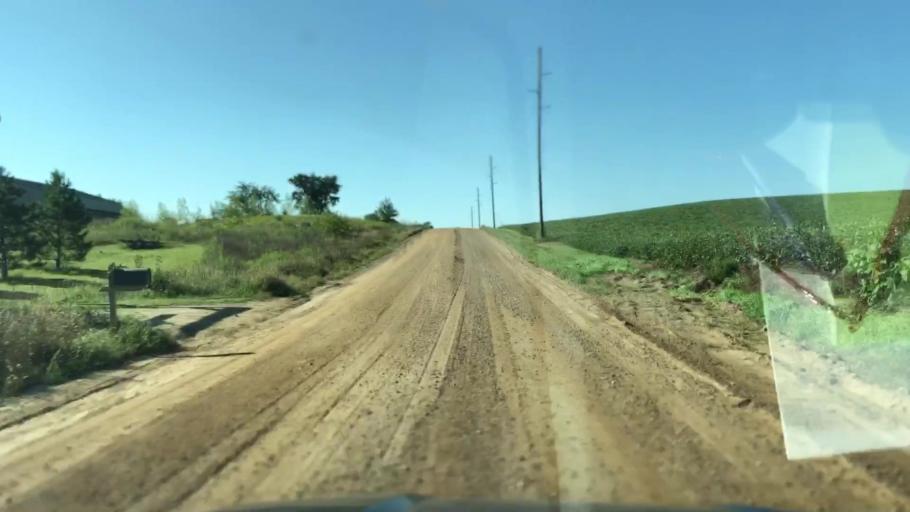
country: US
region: Iowa
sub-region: Woodbury County
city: Sergeant Bluff
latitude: 42.4619
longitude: -96.2526
